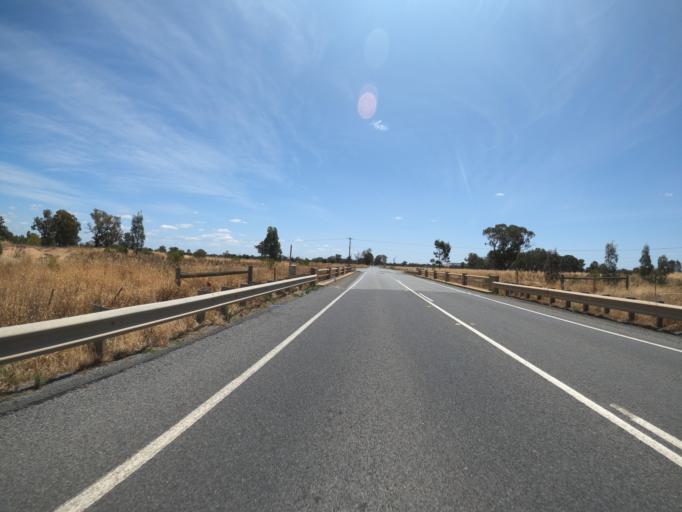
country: AU
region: Victoria
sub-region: Benalla
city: Benalla
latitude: -36.5177
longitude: 146.0330
